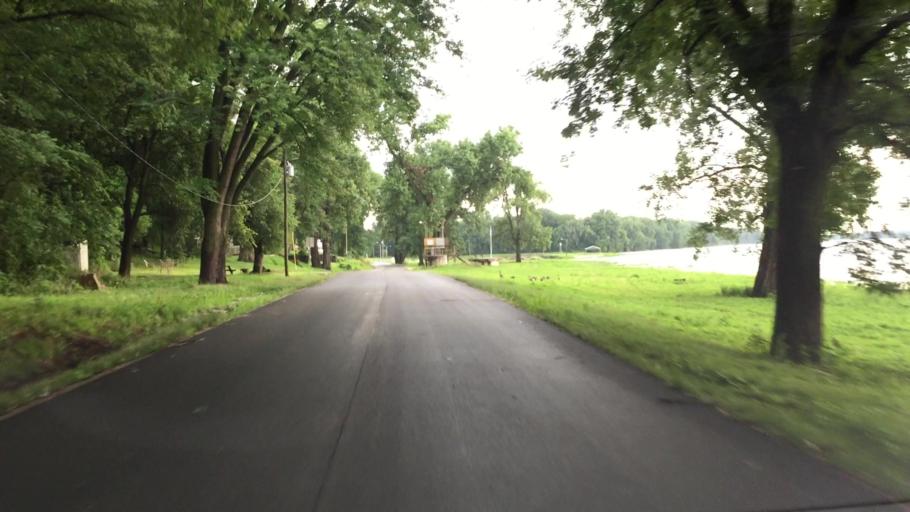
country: US
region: Illinois
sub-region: Hancock County
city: Warsaw
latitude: 40.3573
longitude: -91.4447
